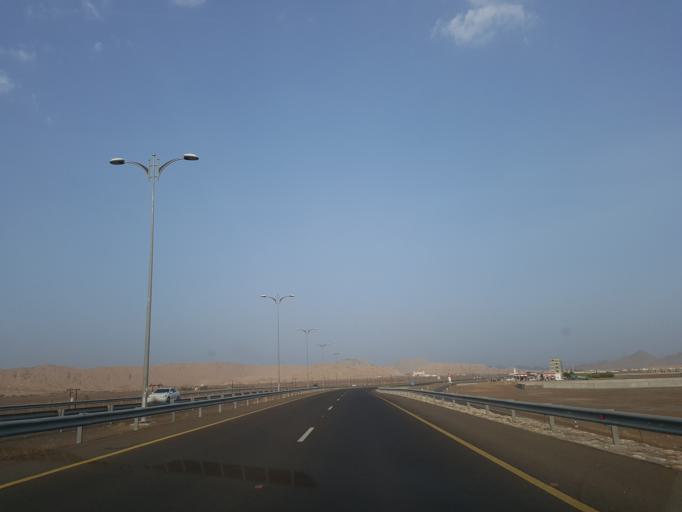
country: OM
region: Al Buraimi
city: Al Buraymi
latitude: 24.2373
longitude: 55.9097
